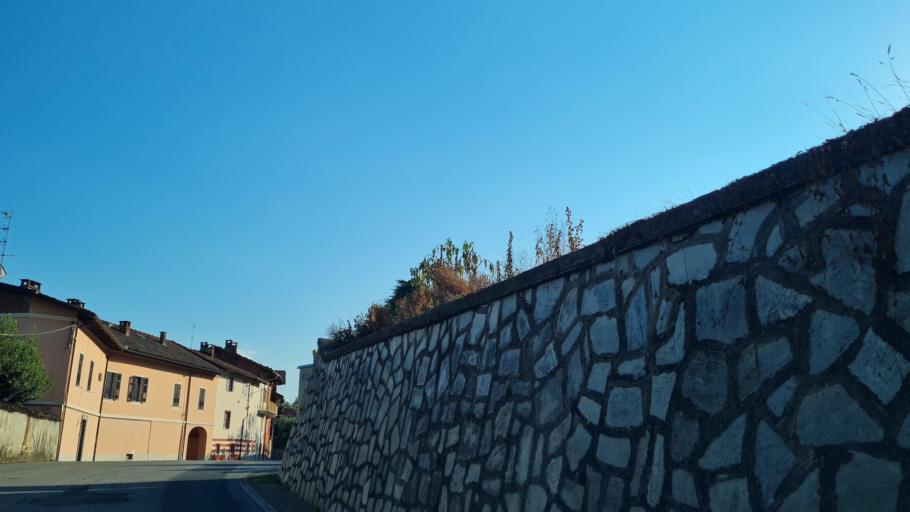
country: IT
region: Piedmont
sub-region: Provincia di Biella
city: Camburzano
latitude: 45.5468
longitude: 8.0046
